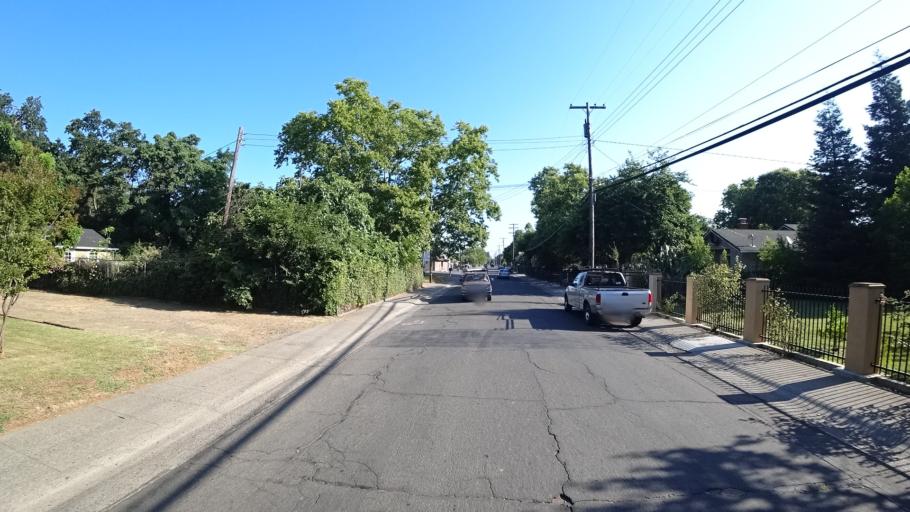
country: US
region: California
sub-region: Sacramento County
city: Florin
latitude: 38.5352
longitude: -121.4191
